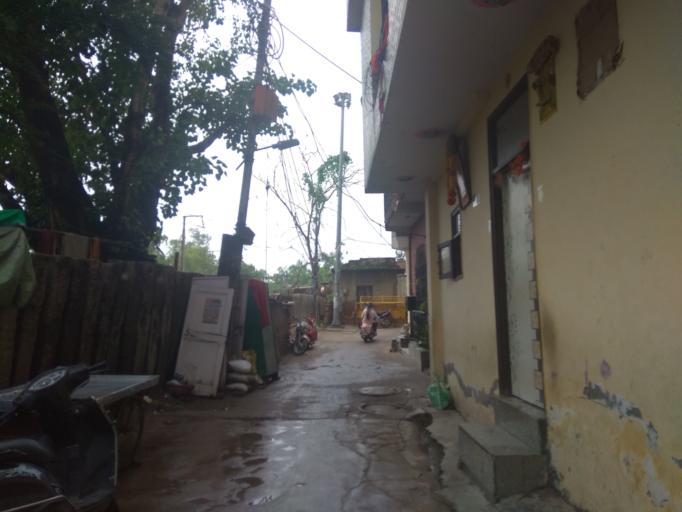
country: IN
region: NCT
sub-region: New Delhi
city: New Delhi
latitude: 28.5757
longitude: 77.2549
